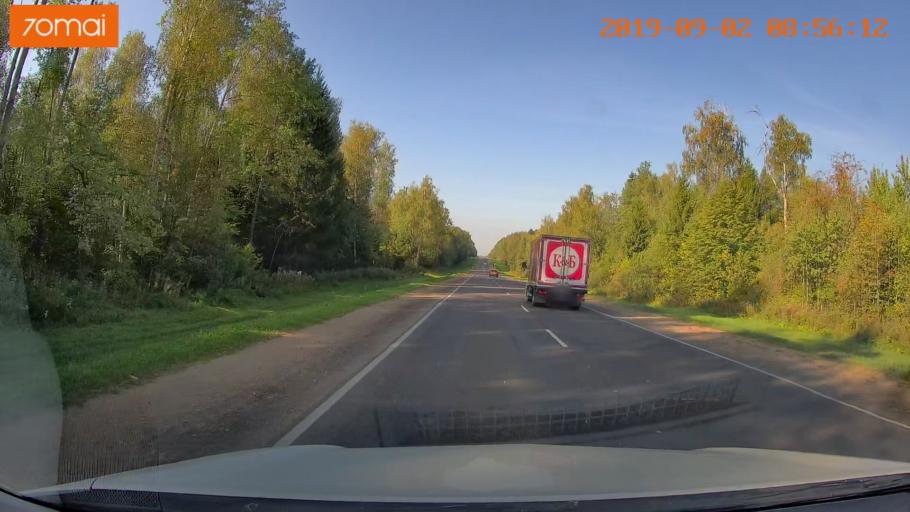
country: RU
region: Kaluga
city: Medyn'
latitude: 54.9474
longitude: 35.7985
